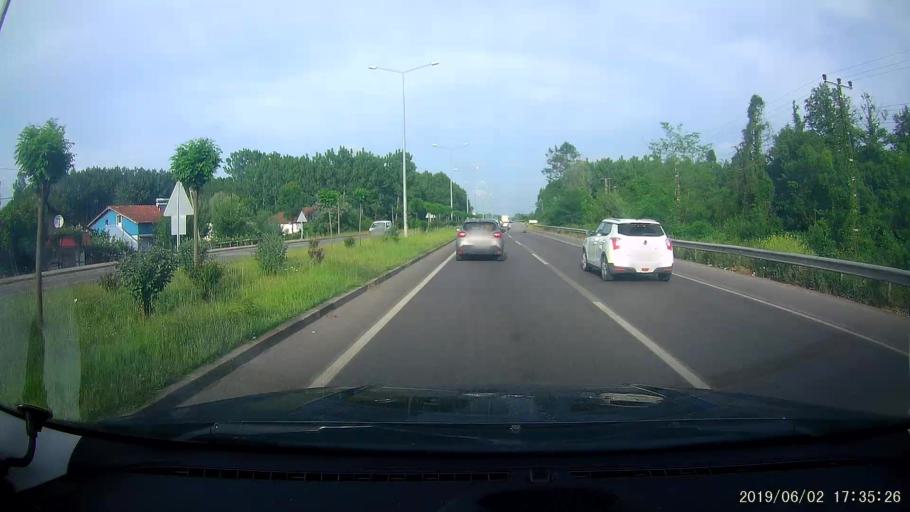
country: TR
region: Samsun
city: Terme
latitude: 41.2196
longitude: 36.8836
